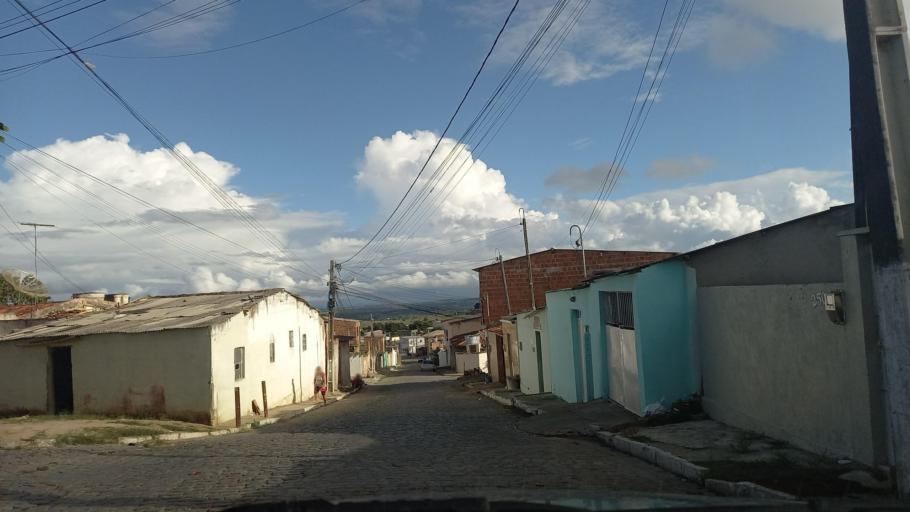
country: BR
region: Pernambuco
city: Garanhuns
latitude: -8.9005
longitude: -36.4985
